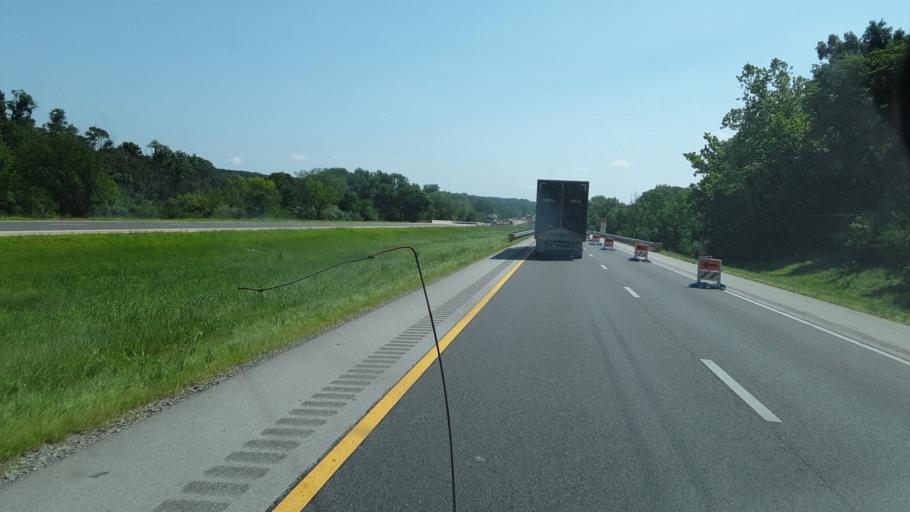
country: US
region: Illinois
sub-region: Cumberland County
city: Toledo
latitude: 39.2011
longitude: -88.2965
